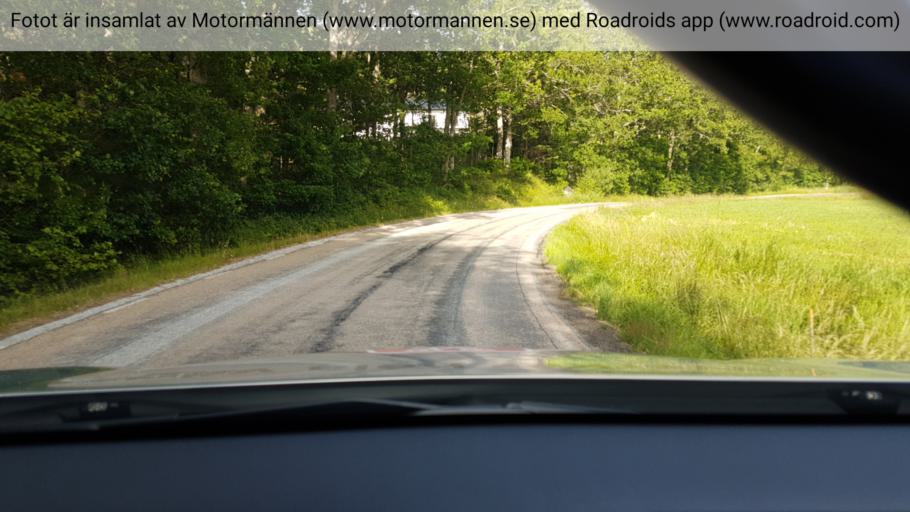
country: SE
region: Vaestra Goetaland
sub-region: Tjorns Kommun
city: Myggenas
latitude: 58.1272
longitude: 11.6844
